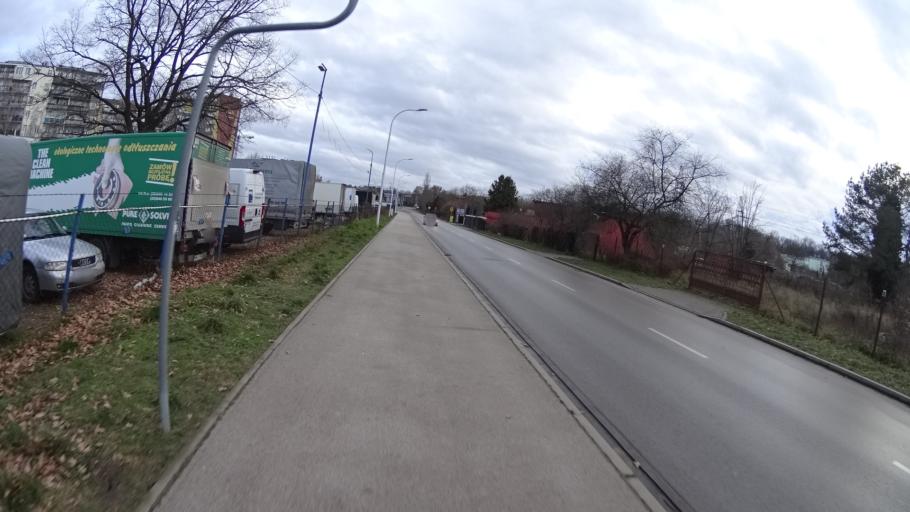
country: PL
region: Masovian Voivodeship
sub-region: Powiat pruszkowski
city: Granica
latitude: 52.1551
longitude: 20.7870
